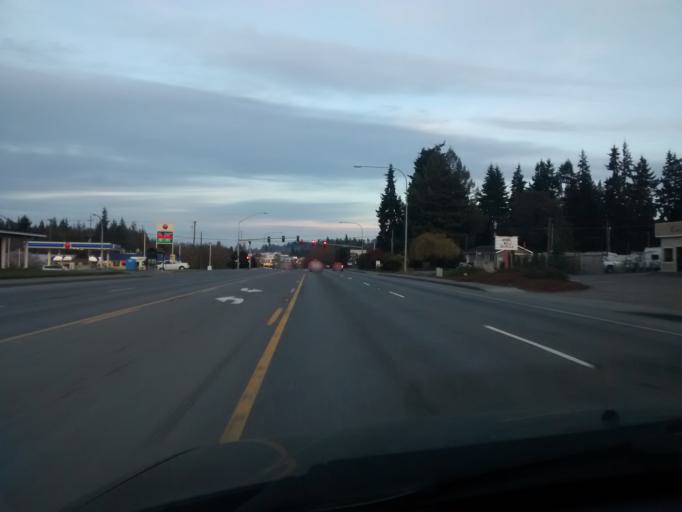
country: US
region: Washington
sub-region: Clallam County
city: Port Angeles East
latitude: 48.1049
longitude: -123.3884
